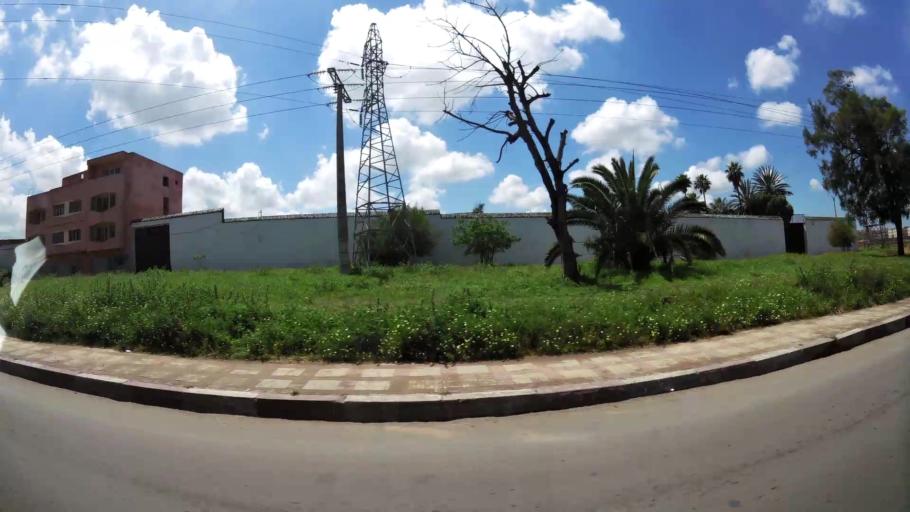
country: MA
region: Grand Casablanca
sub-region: Casablanca
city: Casablanca
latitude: 33.5332
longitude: -7.5717
